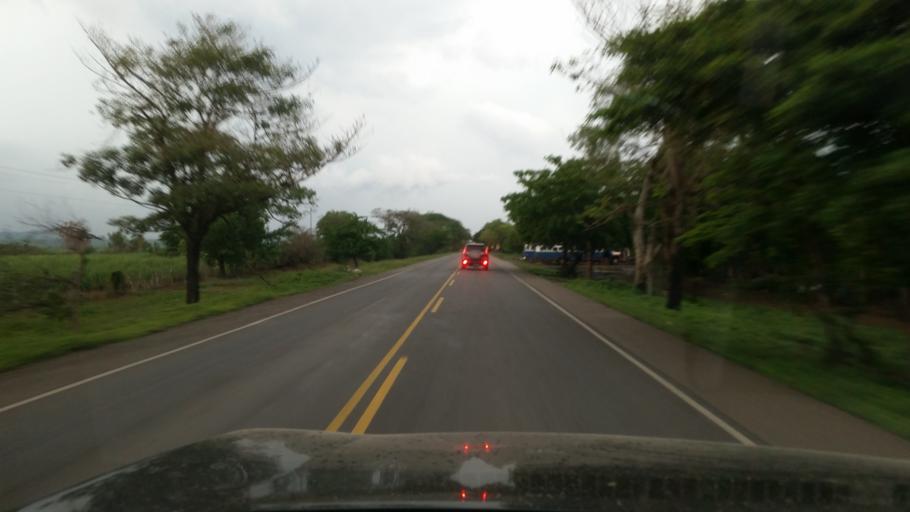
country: NI
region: Chinandega
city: Puerto Morazan
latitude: 12.7682
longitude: -87.0578
